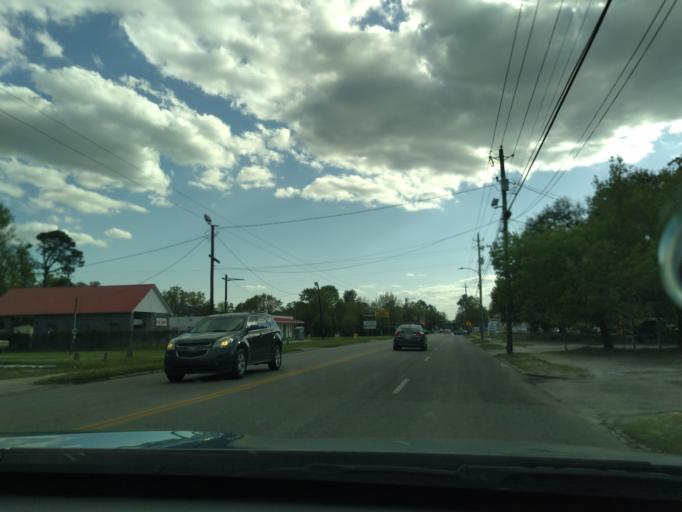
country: US
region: South Carolina
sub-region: Williamsburg County
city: Kingstree
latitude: 33.6805
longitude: -79.8273
